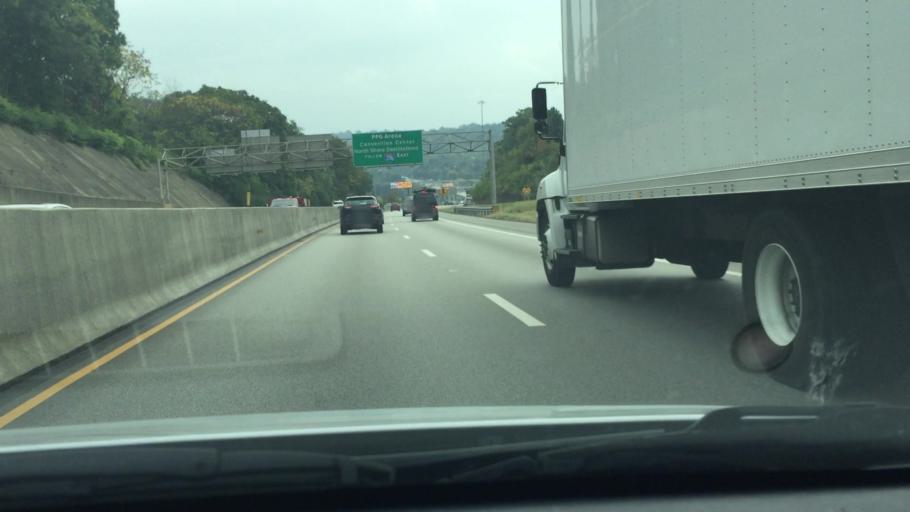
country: US
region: Pennsylvania
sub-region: Allegheny County
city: Carnegie
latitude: 40.4196
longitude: -80.0909
